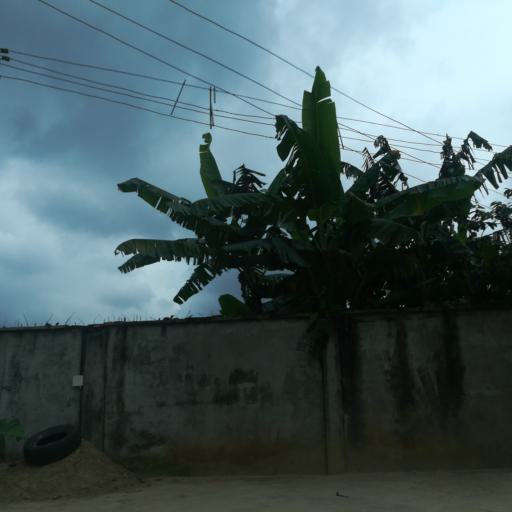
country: NG
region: Rivers
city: Port Harcourt
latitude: 4.8296
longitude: 7.0401
